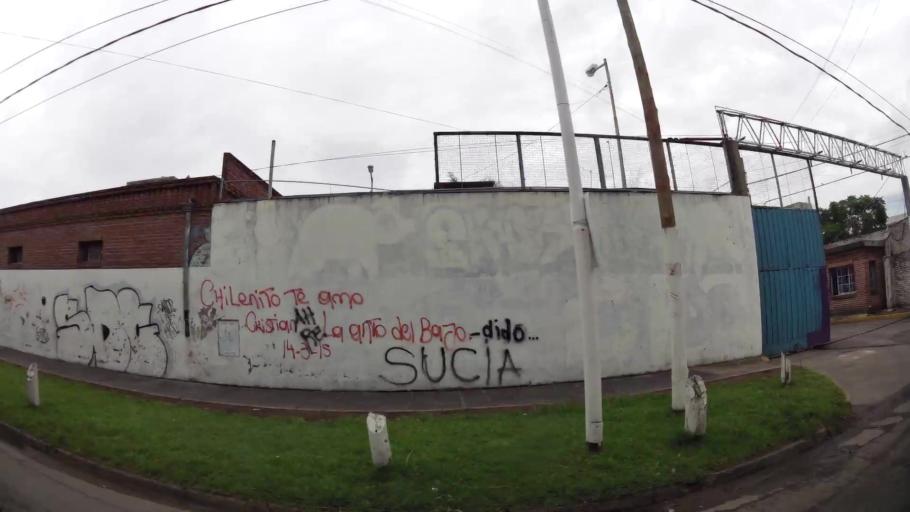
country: AR
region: Buenos Aires
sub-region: Partido de Lanus
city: Lanus
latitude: -34.7301
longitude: -58.3653
